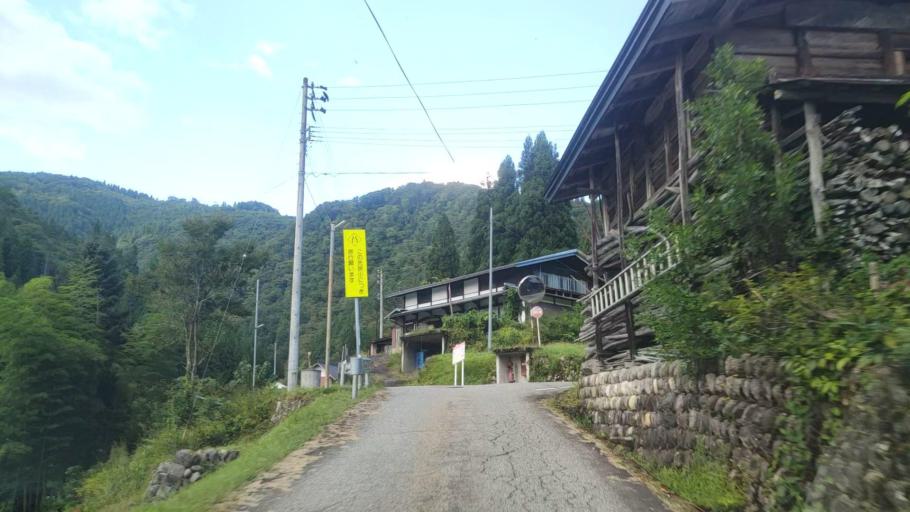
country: JP
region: Gifu
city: Takayama
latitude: 36.3068
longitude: 137.0927
